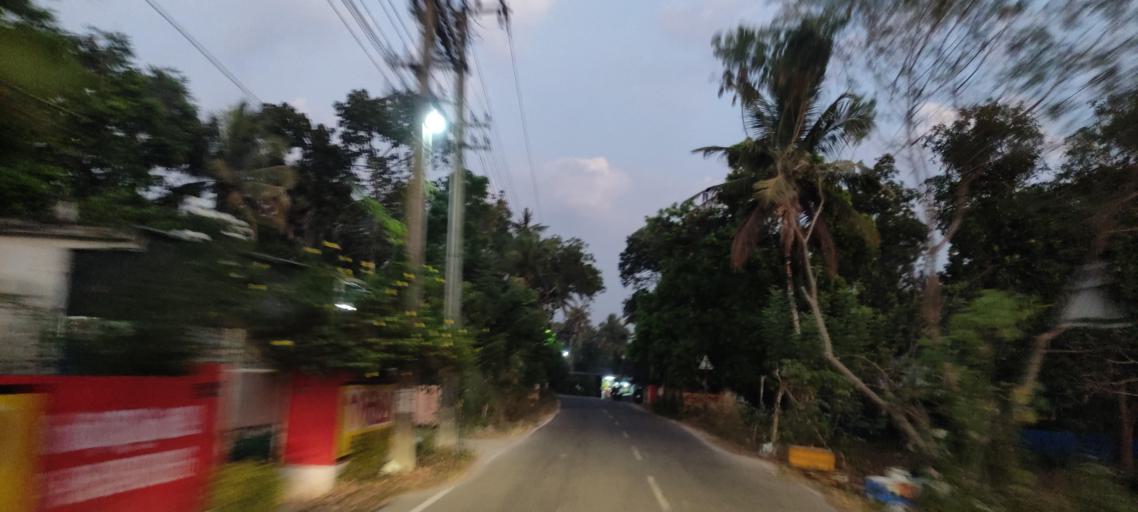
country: IN
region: Kerala
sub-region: Alappuzha
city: Kutiatodu
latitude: 9.7741
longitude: 76.3620
